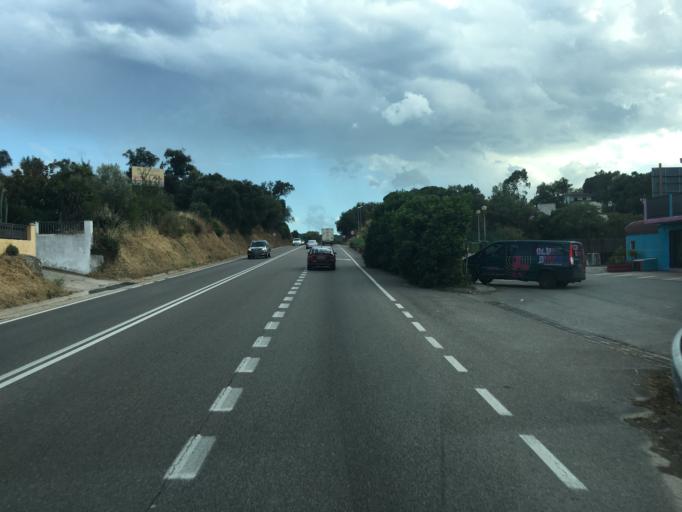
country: ES
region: Catalonia
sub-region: Provincia de Barcelona
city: Tordera
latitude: 41.6897
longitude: 2.7225
